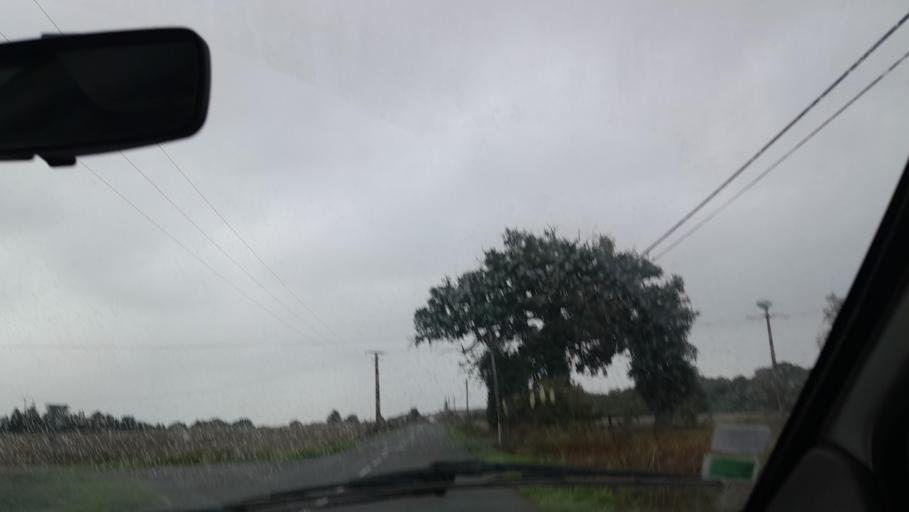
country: FR
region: Pays de la Loire
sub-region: Departement de Maine-et-Loire
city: Pouance
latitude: 47.7293
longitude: -1.1776
